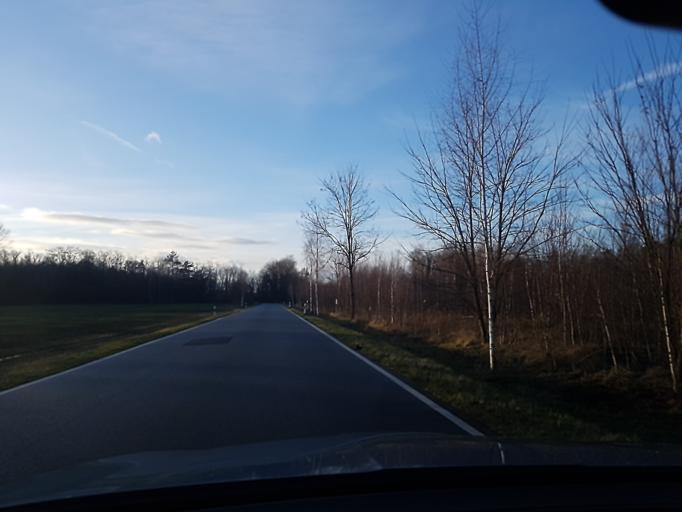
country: DE
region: Brandenburg
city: Trobitz
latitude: 51.5915
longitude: 13.4179
